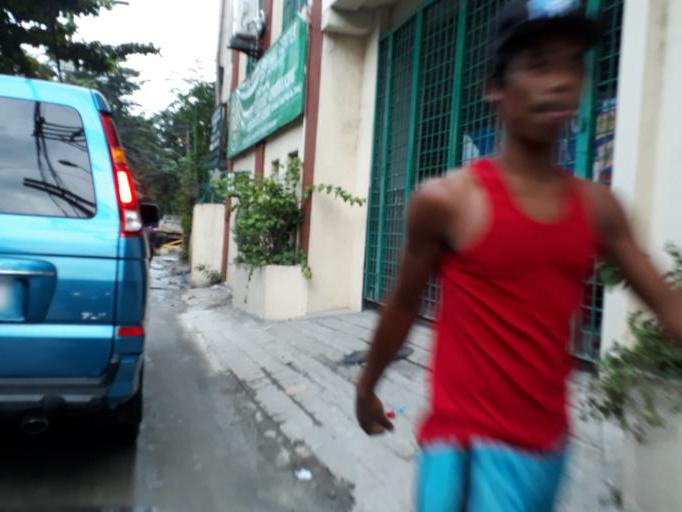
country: PH
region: Calabarzon
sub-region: Province of Rizal
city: Valenzuela
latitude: 14.6944
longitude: 120.9941
